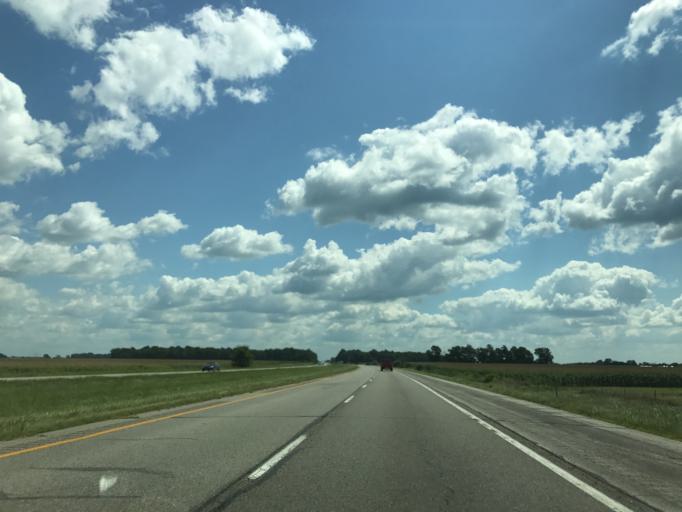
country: US
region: Indiana
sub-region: Marshall County
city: Plymouth
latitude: 41.3343
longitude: -86.2482
